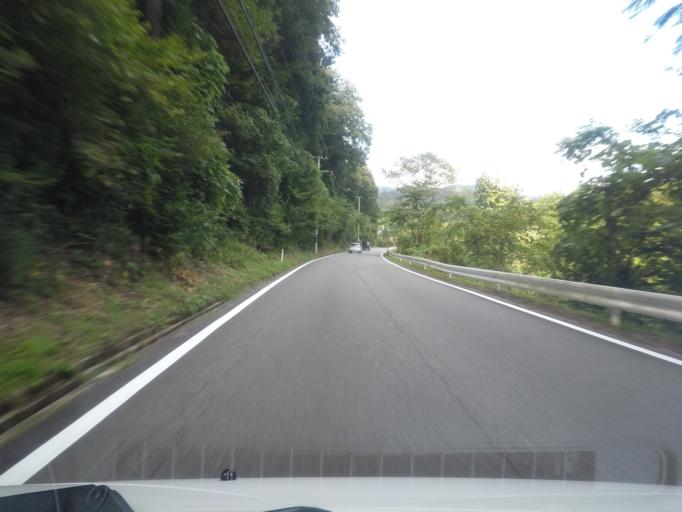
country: JP
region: Fukushima
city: Namie
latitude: 37.5649
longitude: 140.7955
